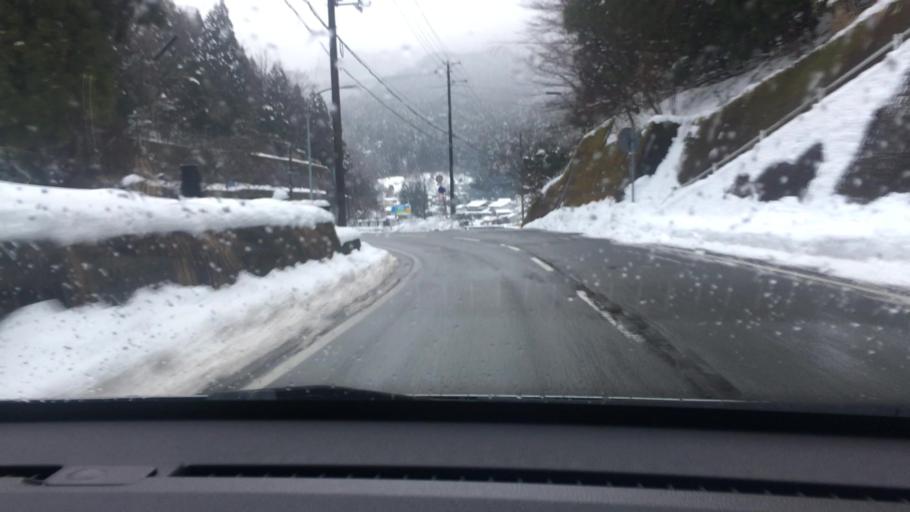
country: JP
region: Hyogo
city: Toyooka
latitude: 35.3664
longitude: 134.5863
